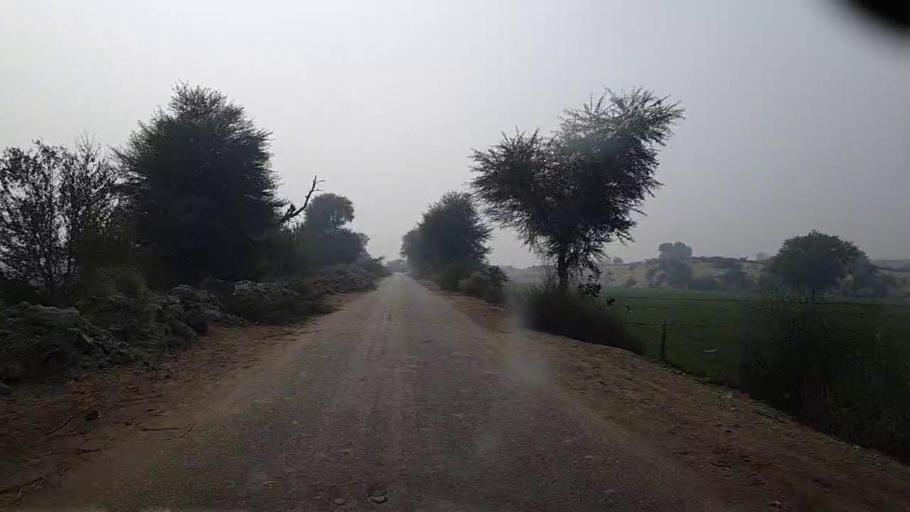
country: PK
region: Sindh
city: Kandiari
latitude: 26.9847
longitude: 68.6030
